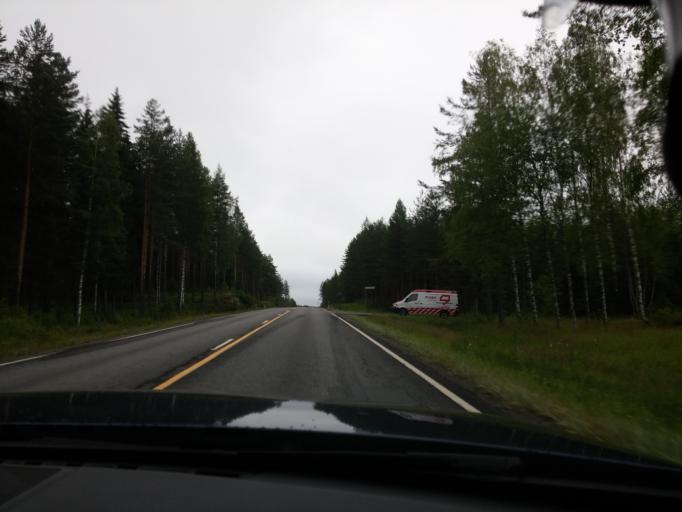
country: FI
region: Pirkanmaa
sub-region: Ylae-Pirkanmaa
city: Vilppula
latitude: 61.9550
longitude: 24.5613
